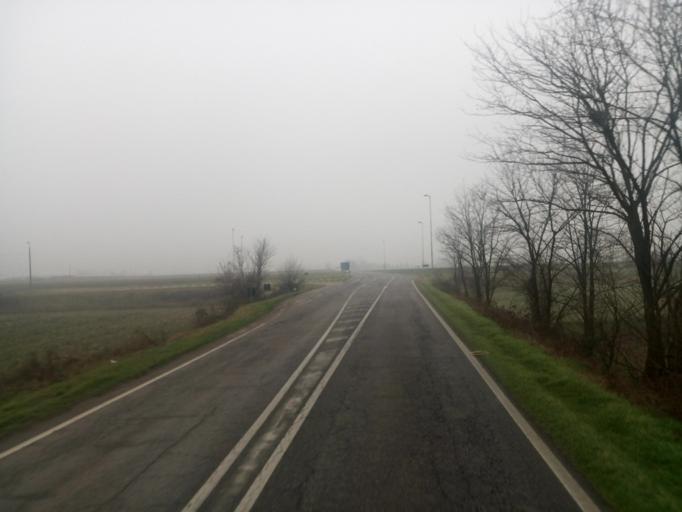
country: IT
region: Lombardy
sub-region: Provincia di Cremona
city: Crotta d'Adda
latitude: 45.1729
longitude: 9.8645
